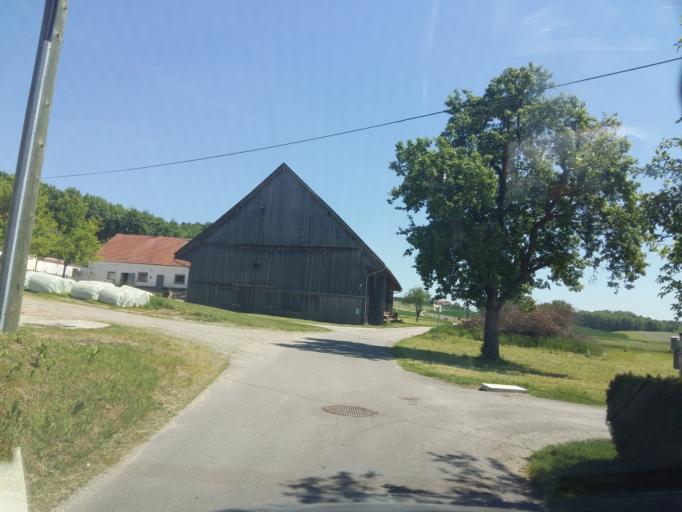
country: AT
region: Upper Austria
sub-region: Politischer Bezirk Scharding
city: Sankt Marienkirchen bei Schaerding
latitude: 48.3768
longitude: 13.4492
